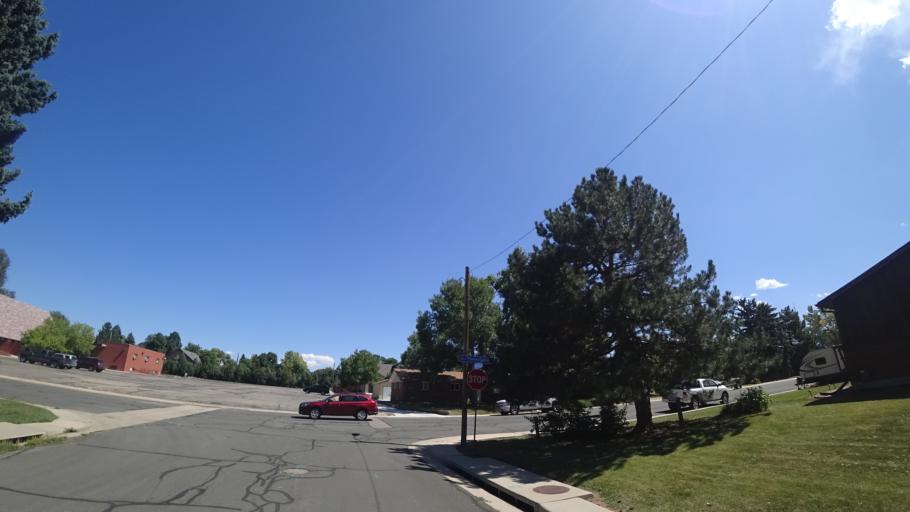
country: US
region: Colorado
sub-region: Arapahoe County
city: Greenwood Village
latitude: 39.6051
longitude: -104.9811
